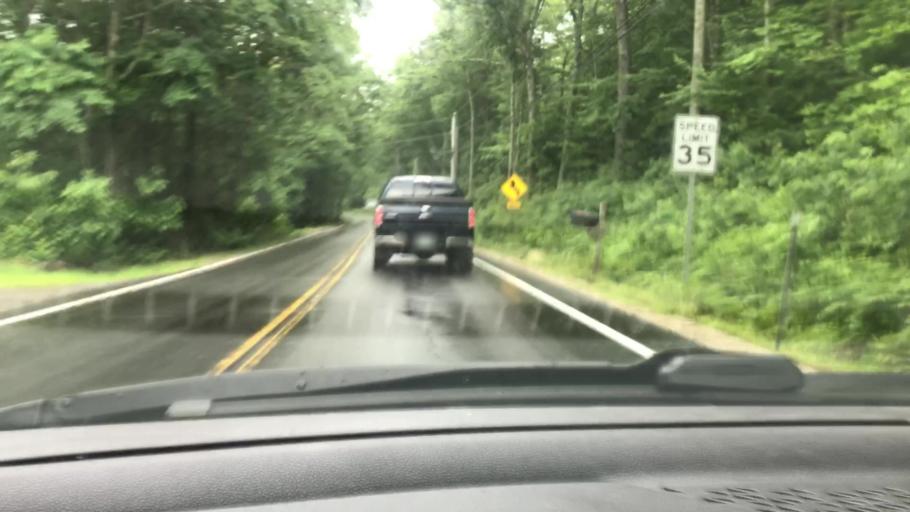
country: US
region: New Hampshire
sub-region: Merrimack County
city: Epsom
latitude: 43.2026
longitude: -71.2743
